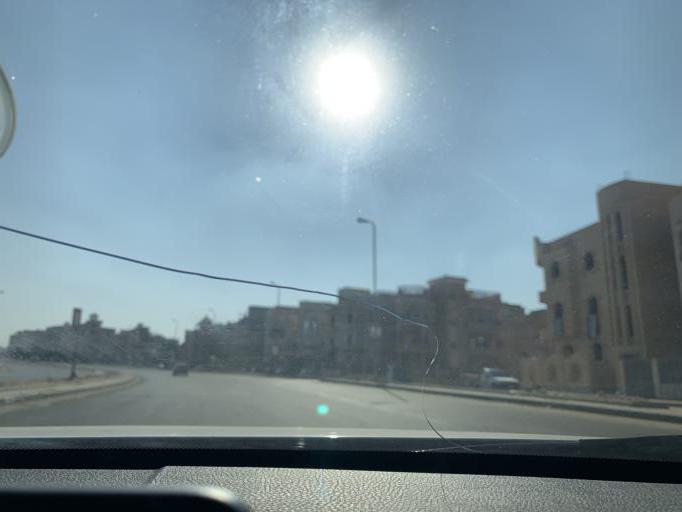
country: EG
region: Muhafazat al Qalyubiyah
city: Al Khankah
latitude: 30.0044
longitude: 31.4810
